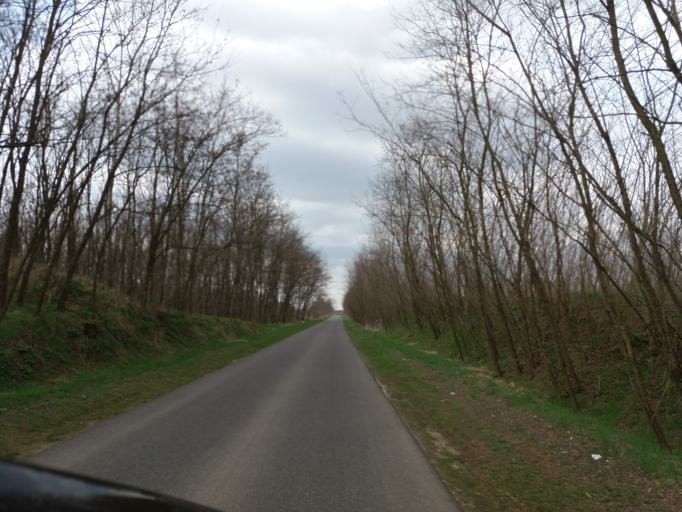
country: HU
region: Szabolcs-Szatmar-Bereg
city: Nyirtass
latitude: 48.0822
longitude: 22.0394
